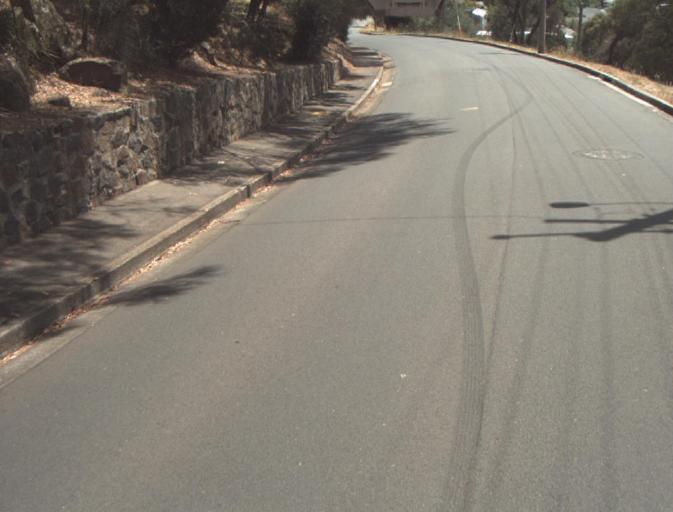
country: AU
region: Tasmania
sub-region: Launceston
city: West Launceston
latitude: -41.4551
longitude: 147.1320
